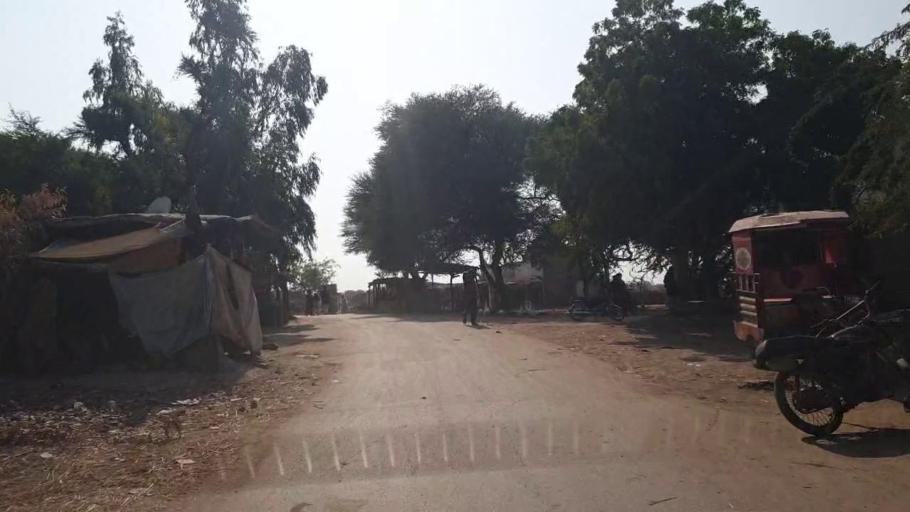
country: PK
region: Sindh
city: Matli
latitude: 24.9833
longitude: 68.6602
